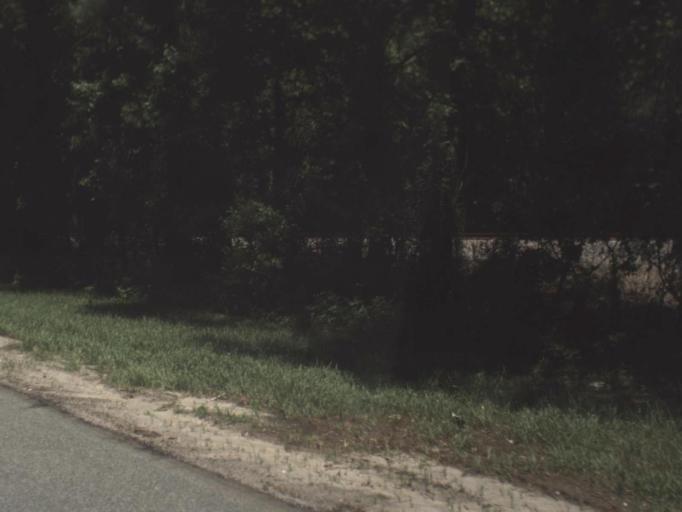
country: US
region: Florida
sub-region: Suwannee County
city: Live Oak
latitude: 30.3653
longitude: -83.1384
